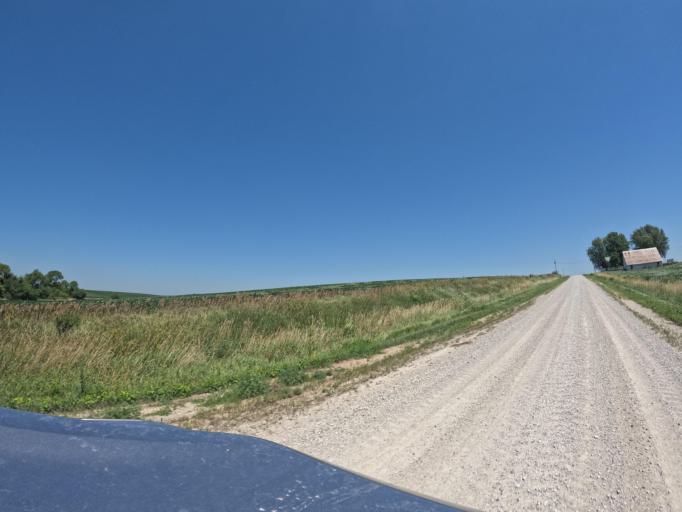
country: US
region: Iowa
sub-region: Keokuk County
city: Sigourney
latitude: 41.4235
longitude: -92.3234
